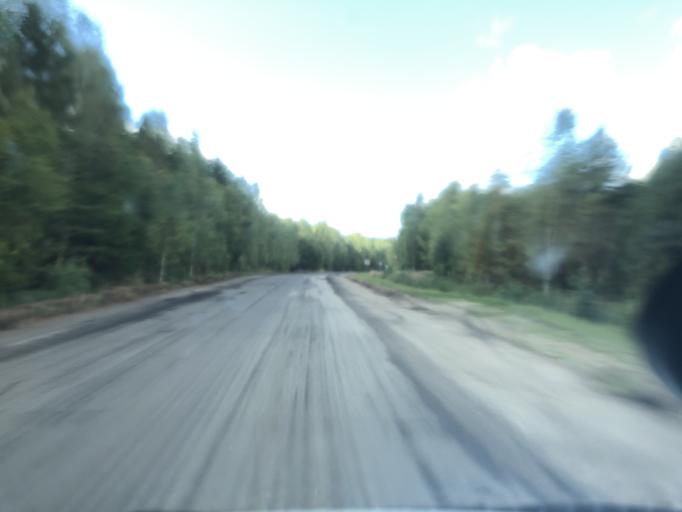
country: RU
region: Jaroslavl
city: Porech'ye-Rybnoye
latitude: 56.9653
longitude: 39.4527
